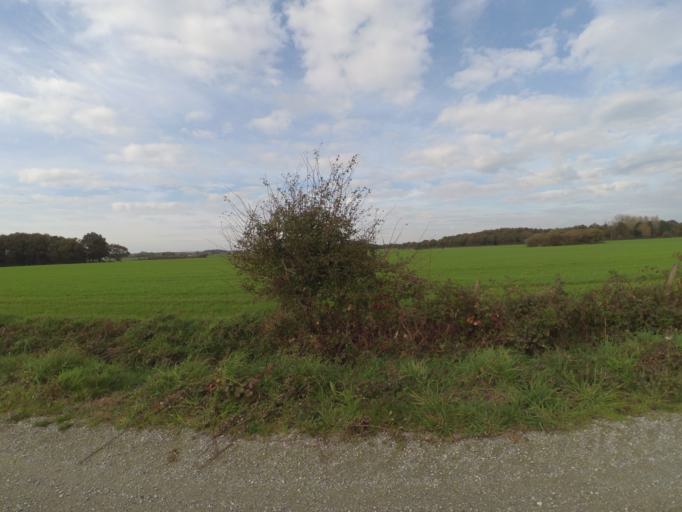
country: FR
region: Pays de la Loire
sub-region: Departement de la Loire-Atlantique
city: La Planche
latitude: 46.9960
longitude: -1.3881
